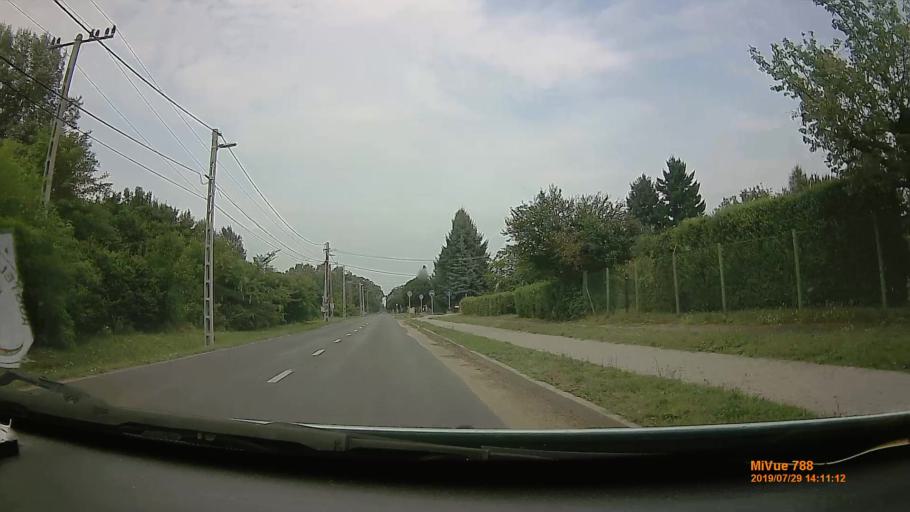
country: HU
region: Somogy
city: Balatonfoldvar
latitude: 46.8520
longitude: 17.8978
